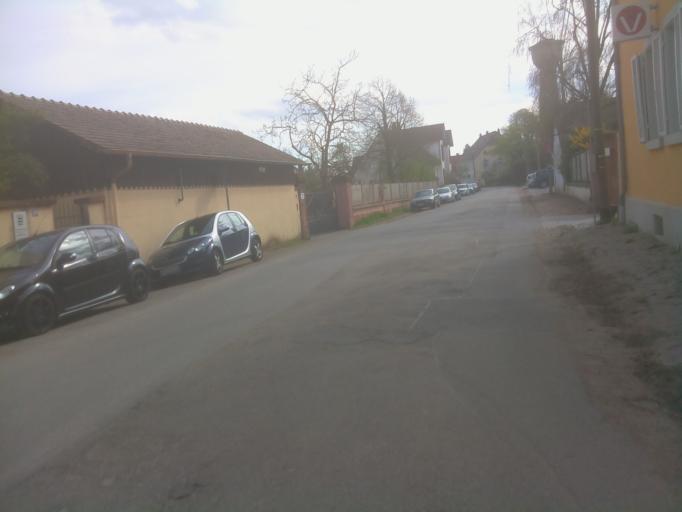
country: DE
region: Hesse
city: Viernheim
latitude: 49.5135
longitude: 8.5770
